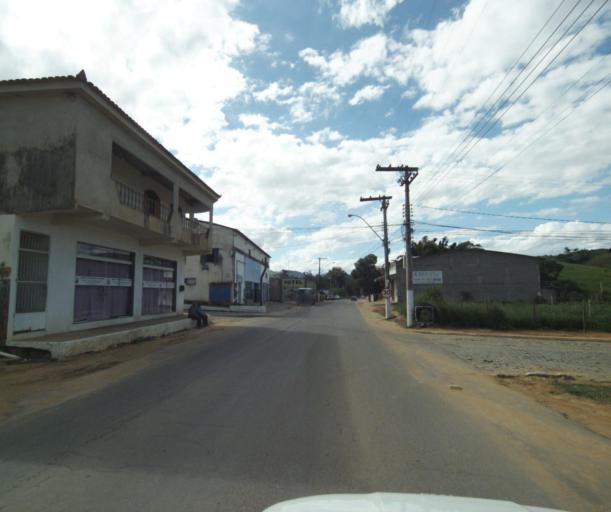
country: BR
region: Espirito Santo
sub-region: Sao Jose Do Calcado
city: Sao Jose do Calcado
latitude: -21.0402
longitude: -41.6524
